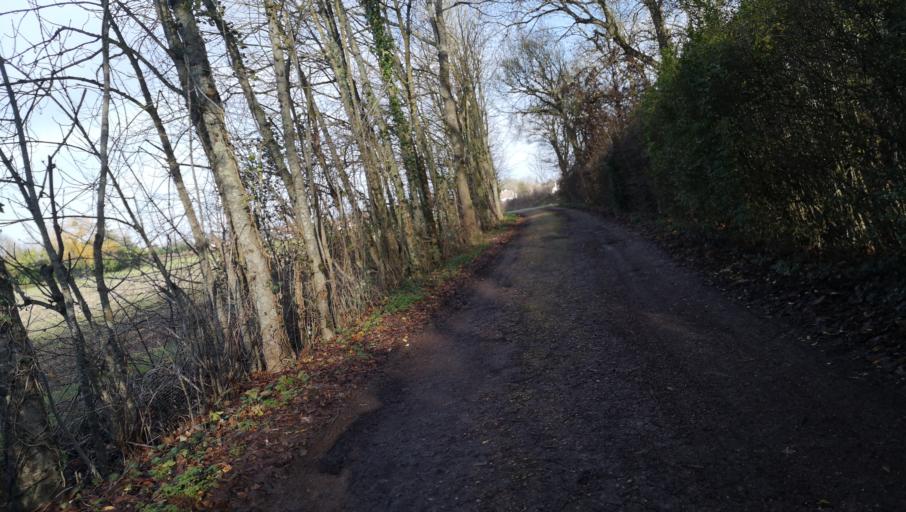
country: FR
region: Centre
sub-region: Departement du Loiret
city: Saint-Pryve-Saint-Mesmin
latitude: 47.8722
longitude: 1.8674
